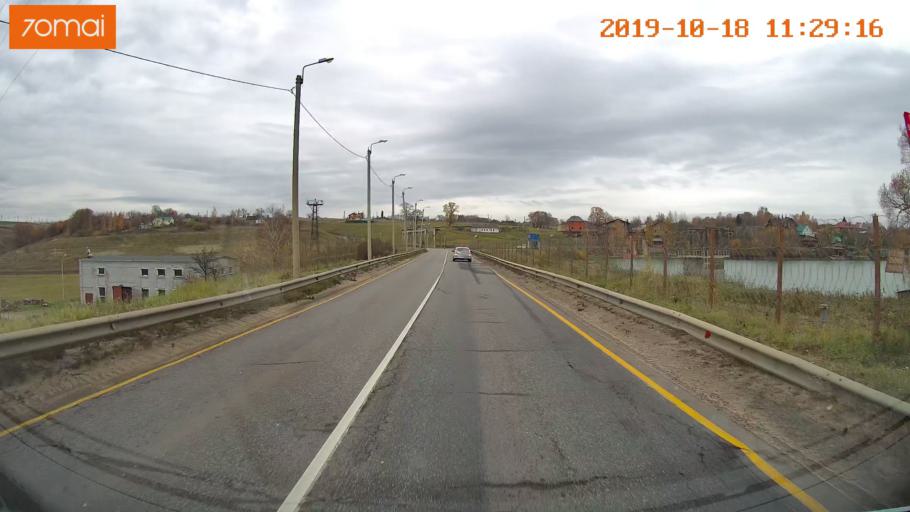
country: RU
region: Rjazan
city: Oktyabr'skiy
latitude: 54.1570
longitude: 38.6750
